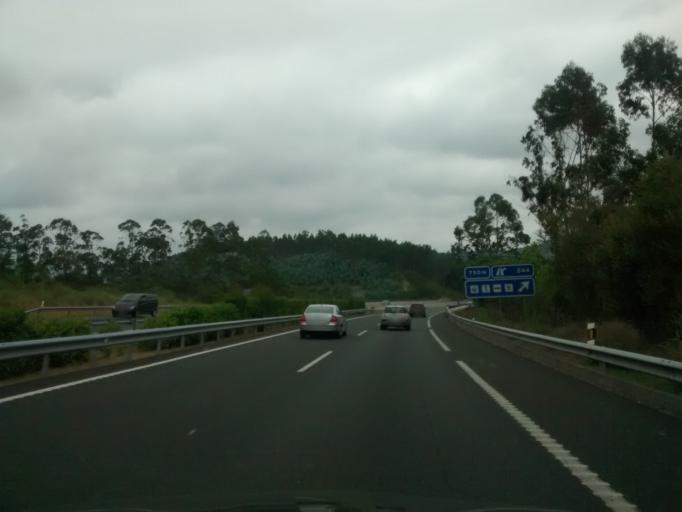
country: ES
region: Cantabria
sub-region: Provincia de Cantabria
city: Luzmela
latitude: 43.3229
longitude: -4.1785
